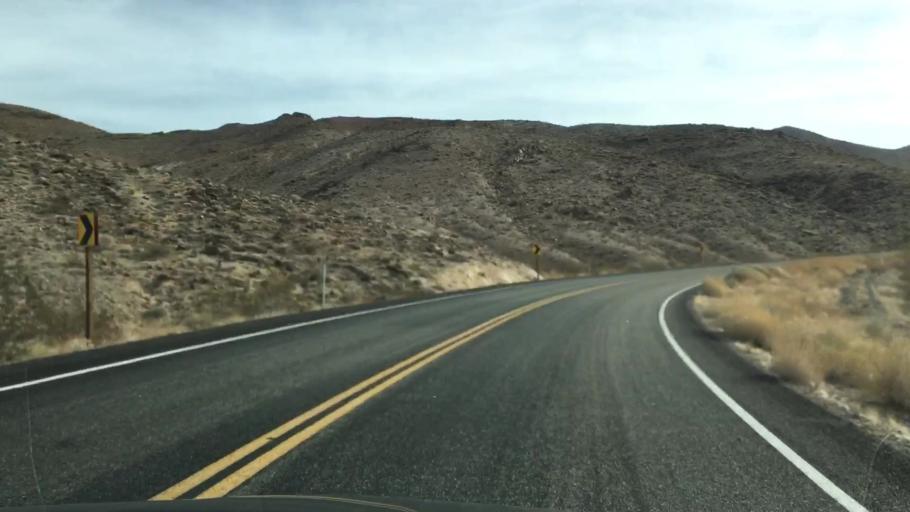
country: US
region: Nevada
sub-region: Nye County
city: Beatty
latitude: 36.7482
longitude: -116.9513
